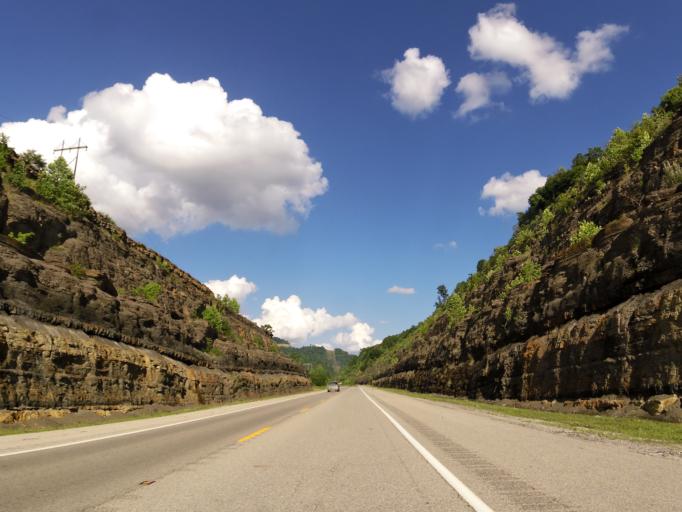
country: US
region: Kentucky
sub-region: Harlan County
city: Harlan
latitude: 36.7818
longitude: -83.2346
